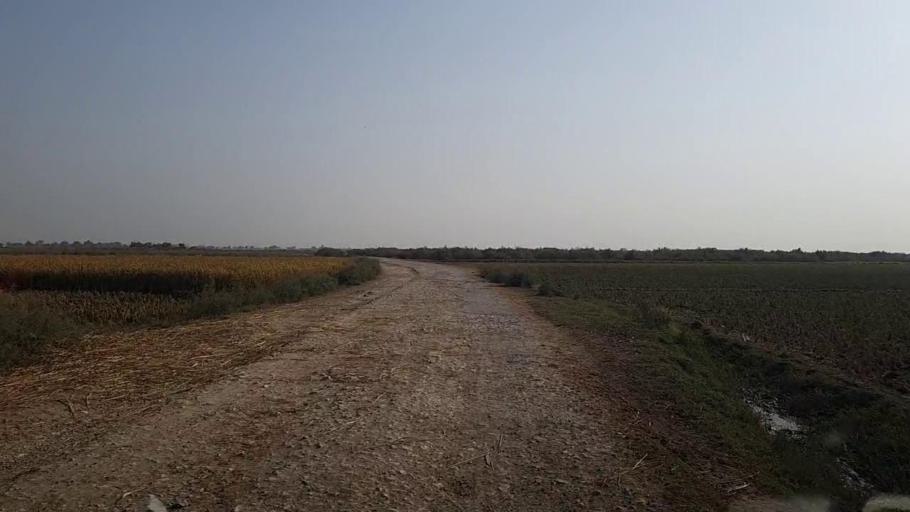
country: PK
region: Sindh
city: Kandhkot
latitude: 28.2967
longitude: 69.2524
